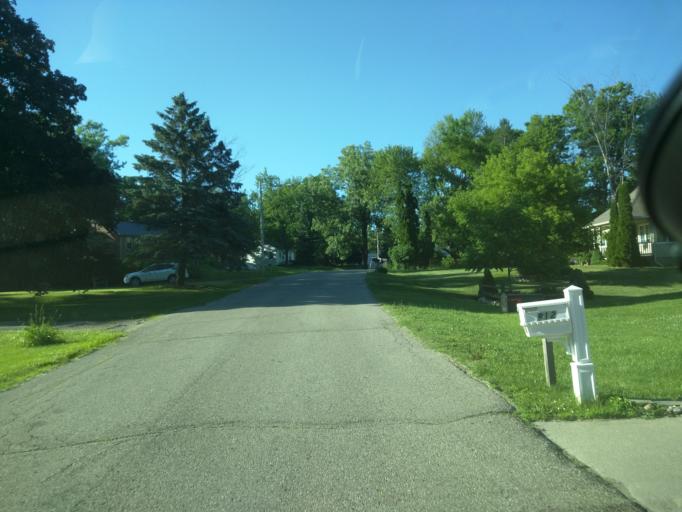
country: US
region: Michigan
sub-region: Ingham County
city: Edgemont Park
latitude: 42.7434
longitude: -84.5948
